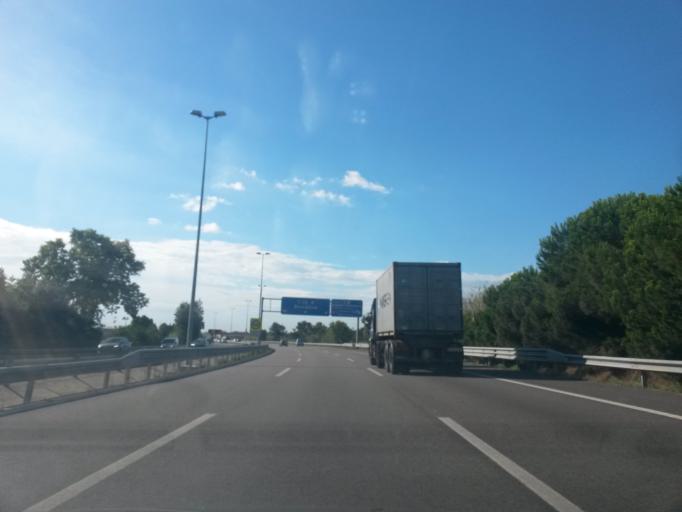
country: ES
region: Catalonia
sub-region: Provincia de Barcelona
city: Argentona
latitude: 41.5409
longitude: 2.4140
